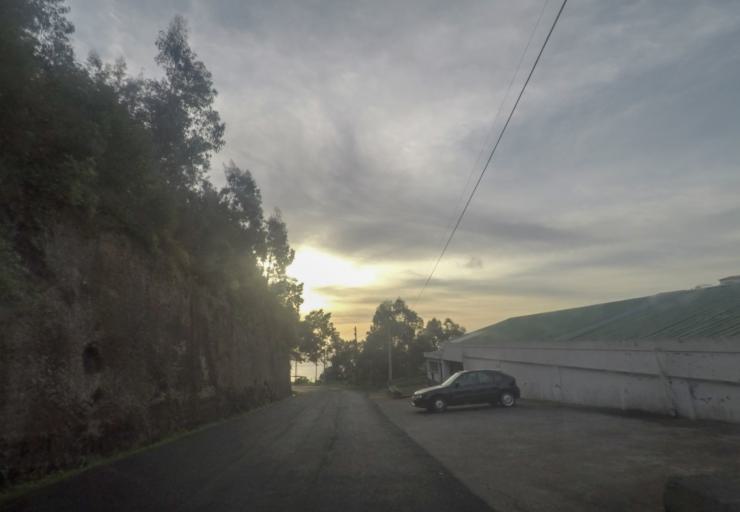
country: PT
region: Madeira
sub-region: Funchal
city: Nossa Senhora do Monte
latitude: 32.6586
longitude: -16.8746
